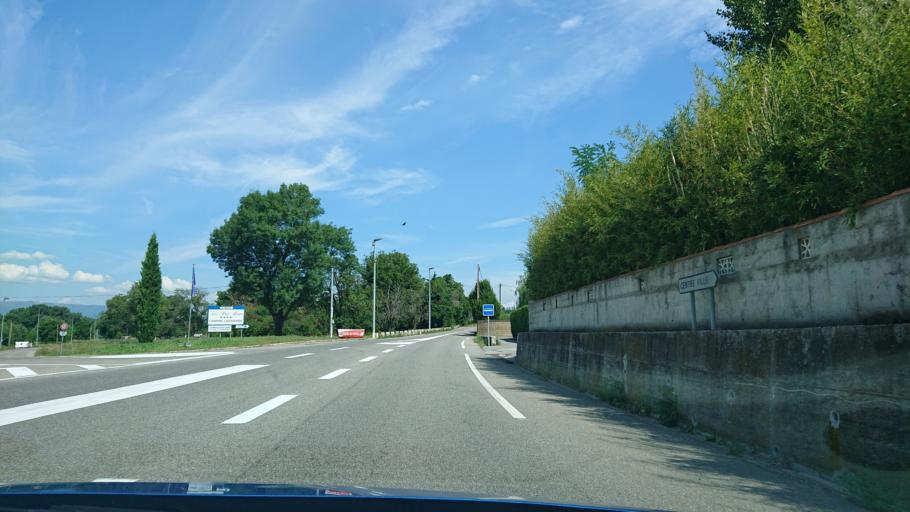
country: FR
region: Provence-Alpes-Cote d'Azur
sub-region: Departement des Alpes-de-Haute-Provence
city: Sisteron
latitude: 44.2114
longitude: 5.9409
